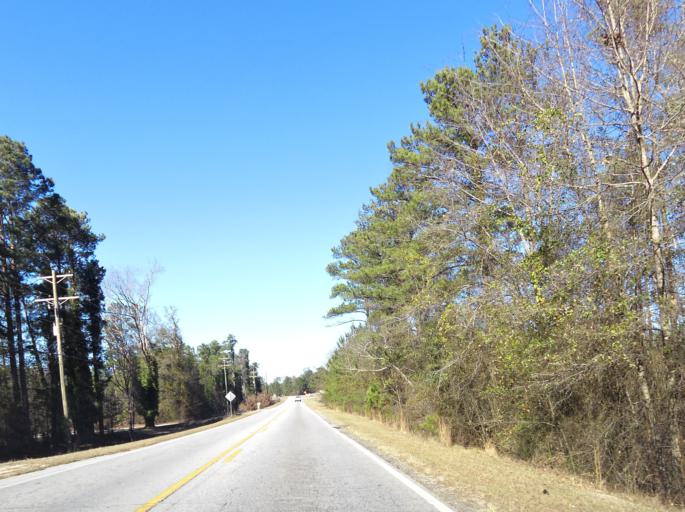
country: US
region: Georgia
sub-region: Bibb County
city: West Point
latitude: 32.7516
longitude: -83.7424
